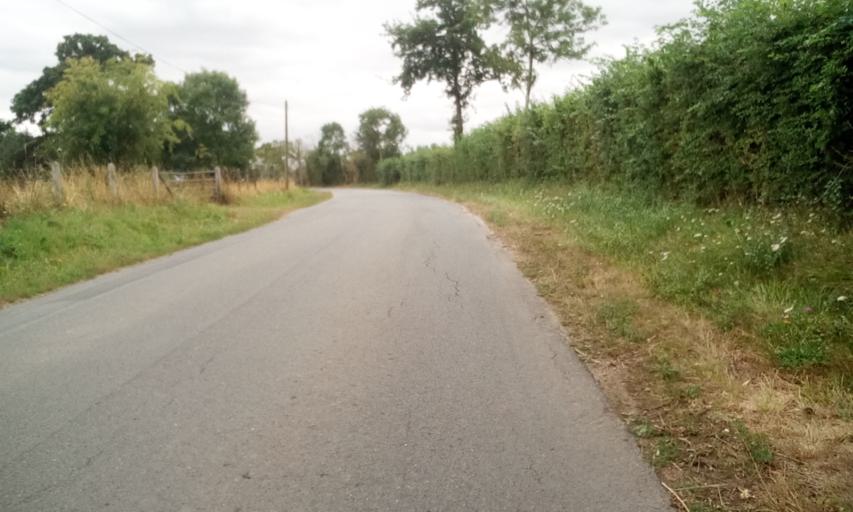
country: FR
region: Lower Normandy
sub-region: Departement du Calvados
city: Troarn
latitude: 49.1949
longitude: -0.1800
